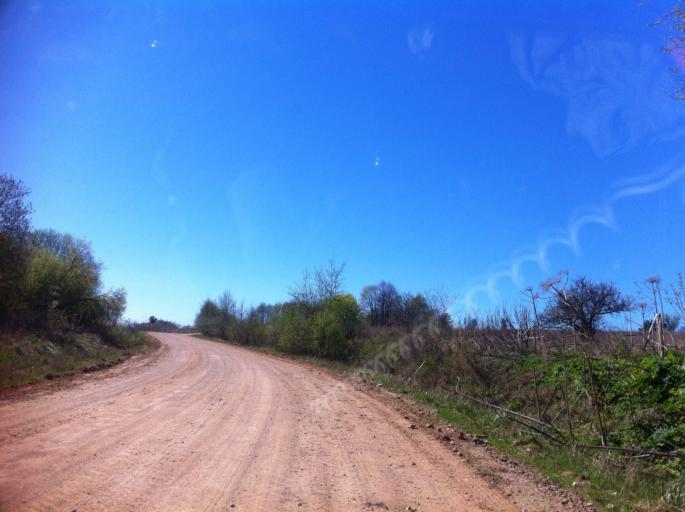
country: RU
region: Pskov
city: Izborsk
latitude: 57.8053
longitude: 27.9734
